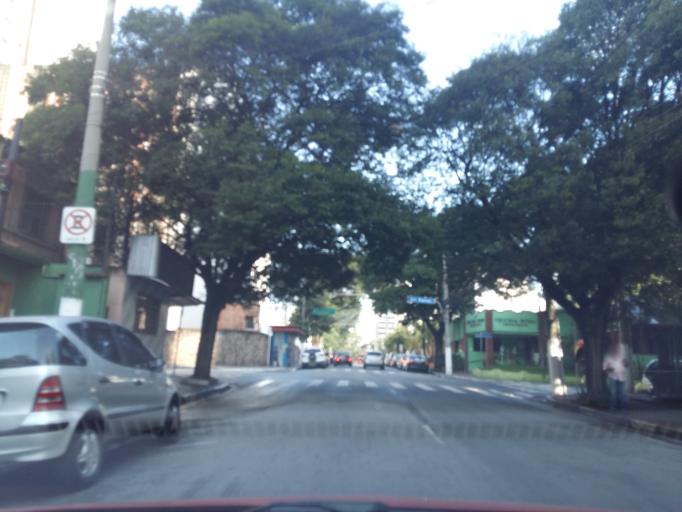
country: BR
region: Sao Paulo
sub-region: Sao Paulo
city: Sao Paulo
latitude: -23.6162
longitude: -46.6790
